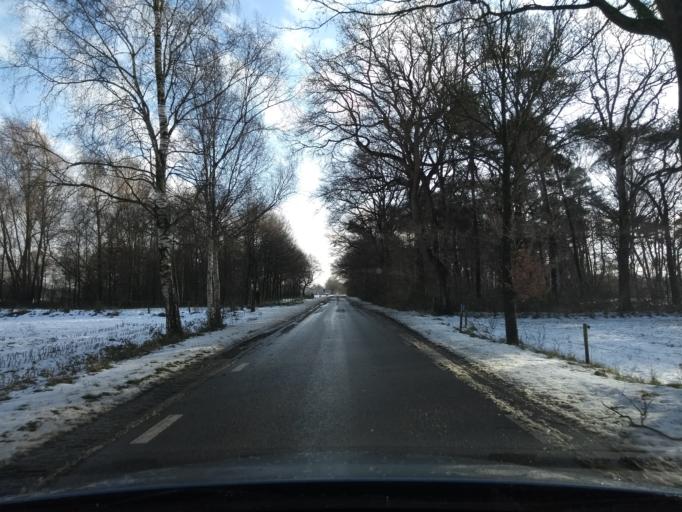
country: NL
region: Gelderland
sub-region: Gemeente Bronckhorst
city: Zelhem
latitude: 52.0355
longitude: 6.3418
